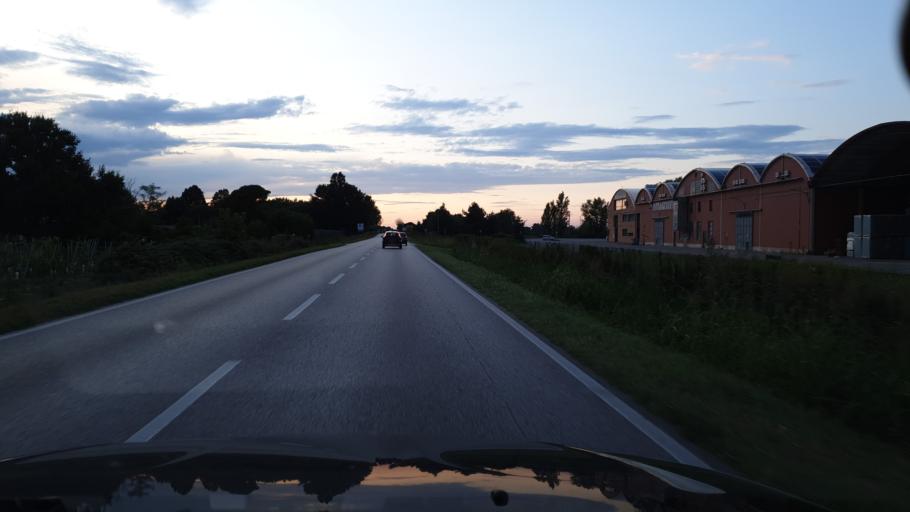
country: IT
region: Emilia-Romagna
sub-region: Provincia di Ravenna
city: Fornace Zarattini
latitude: 44.4326
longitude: 12.1488
